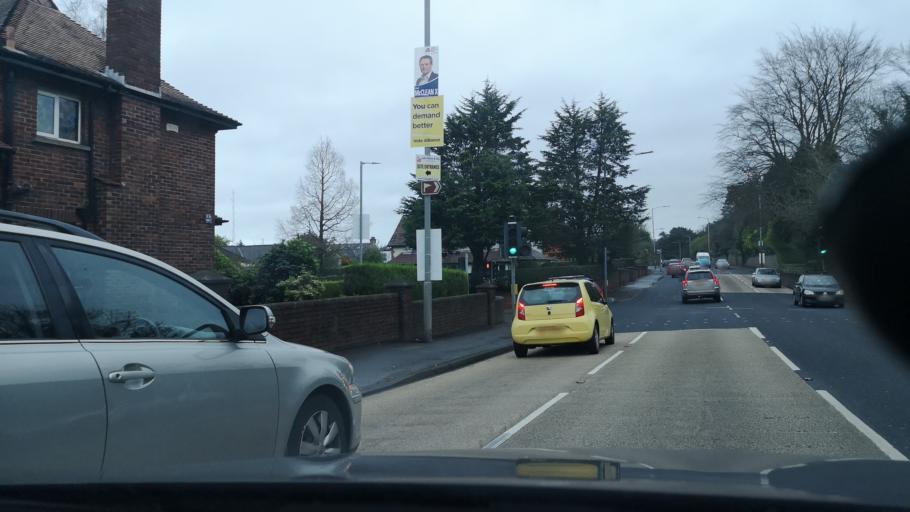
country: GB
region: Northern Ireland
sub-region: Castlereagh District
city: Castlereagh
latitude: 54.5861
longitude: -5.8606
